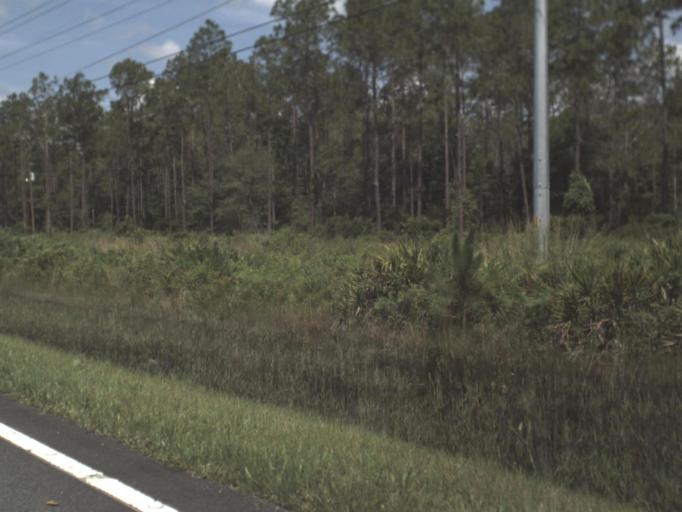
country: US
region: Florida
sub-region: Levy County
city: Chiefland
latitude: 29.3083
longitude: -82.8017
